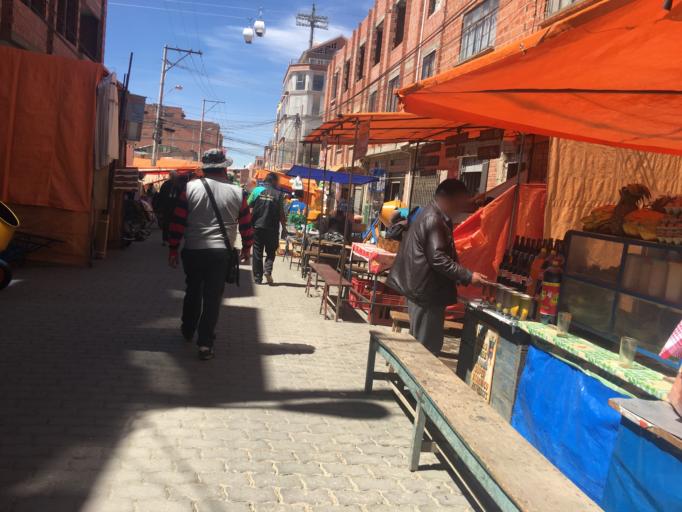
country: BO
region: La Paz
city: La Paz
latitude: -16.4953
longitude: -68.1695
